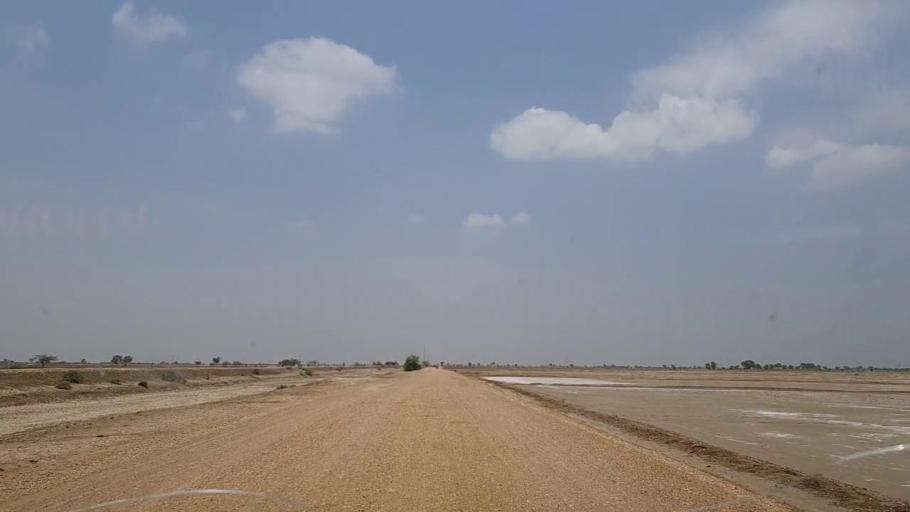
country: PK
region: Sindh
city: Johi
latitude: 26.7669
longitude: 67.6598
